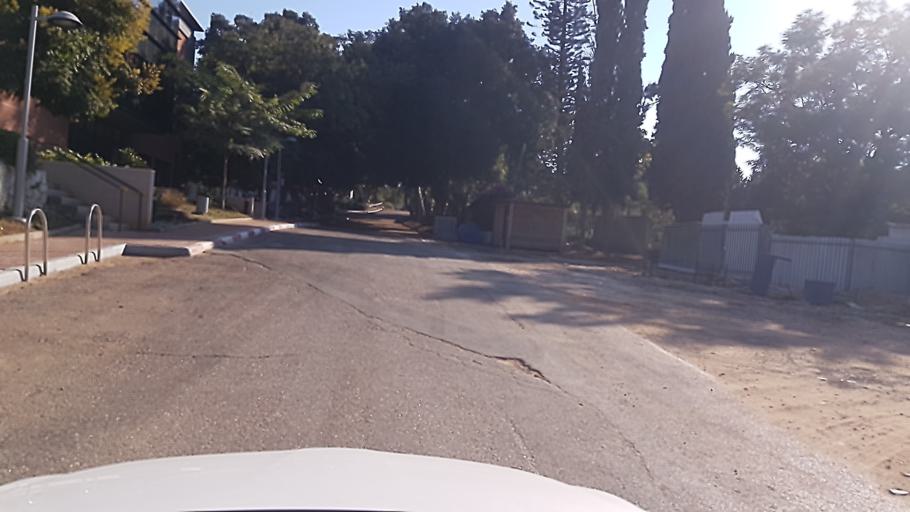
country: IL
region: Central District
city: Kfar Saba
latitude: 32.2026
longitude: 34.9282
